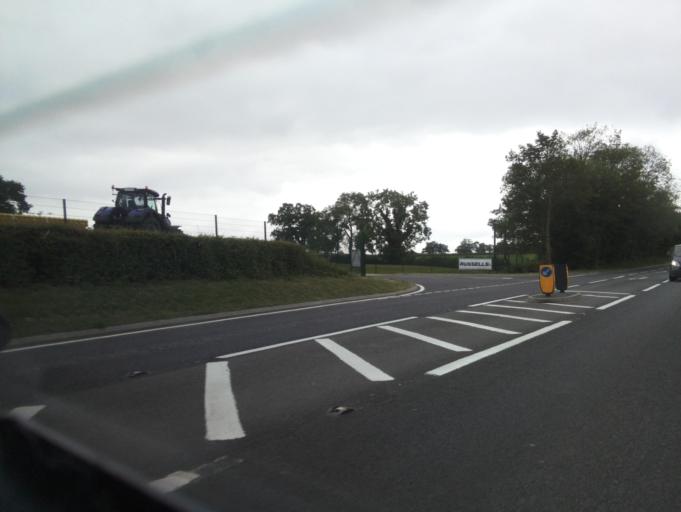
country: GB
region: England
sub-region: Derbyshire
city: Rodsley
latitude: 52.9206
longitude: -1.7610
